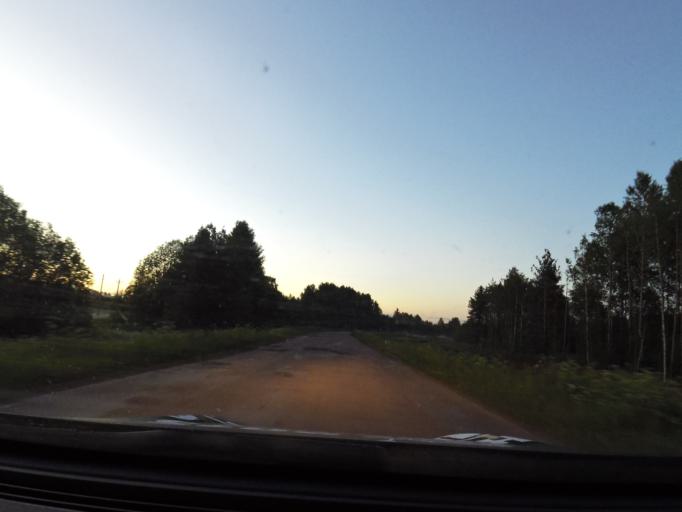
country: RU
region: Vologda
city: Vytegra
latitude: 61.0001
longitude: 36.3809
